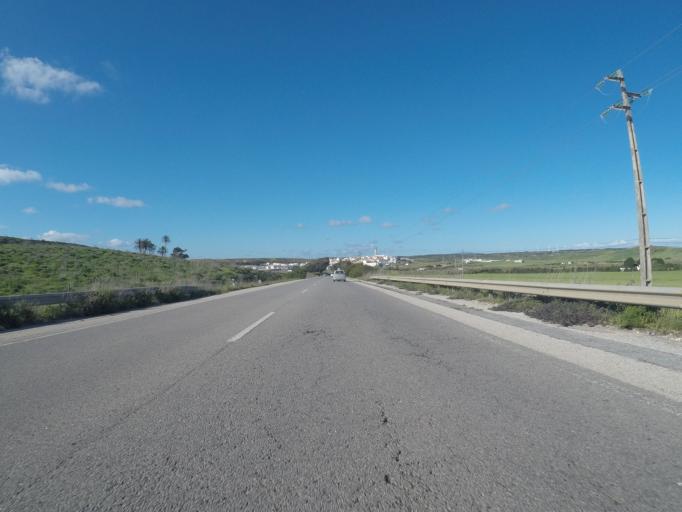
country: PT
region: Faro
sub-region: Vila do Bispo
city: Vila do Bispo
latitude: 37.0746
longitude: -8.9161
